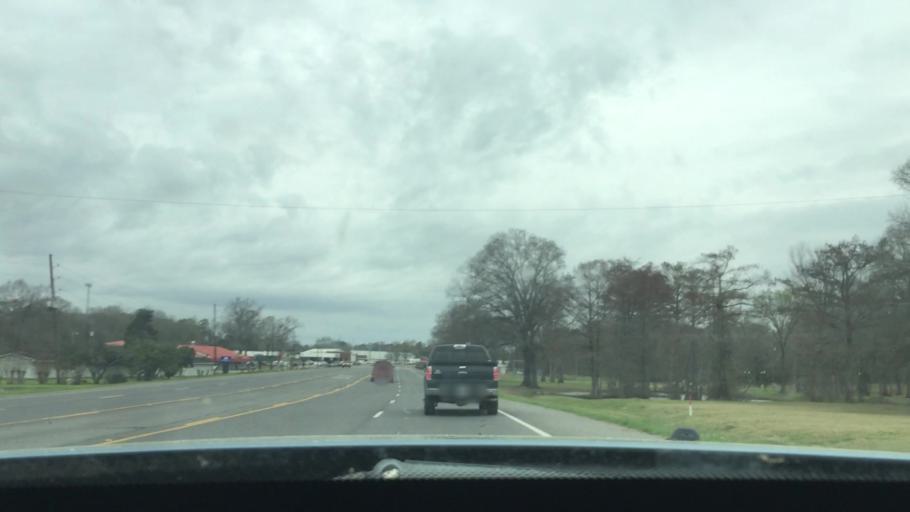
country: US
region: Louisiana
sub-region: Franklin Parish
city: Winnsboro
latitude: 32.1534
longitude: -91.7088
